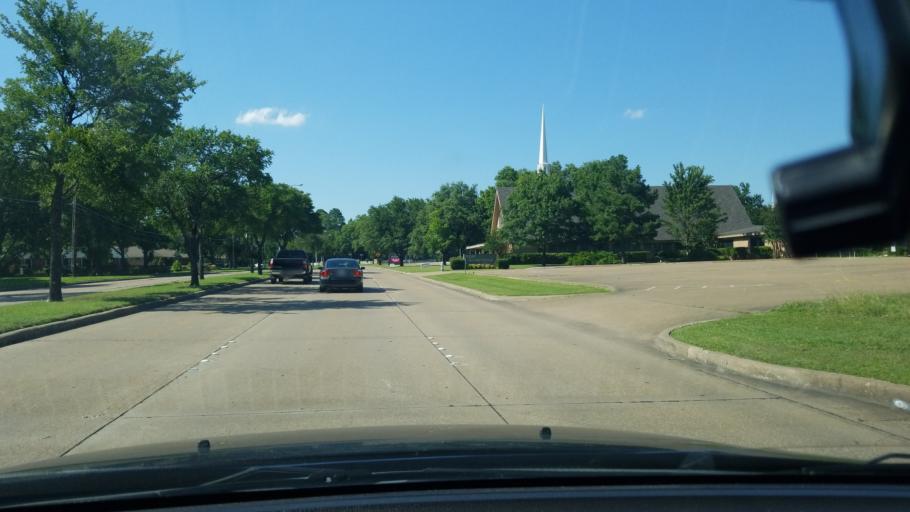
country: US
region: Texas
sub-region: Dallas County
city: Mesquite
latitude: 32.7529
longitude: -96.5965
